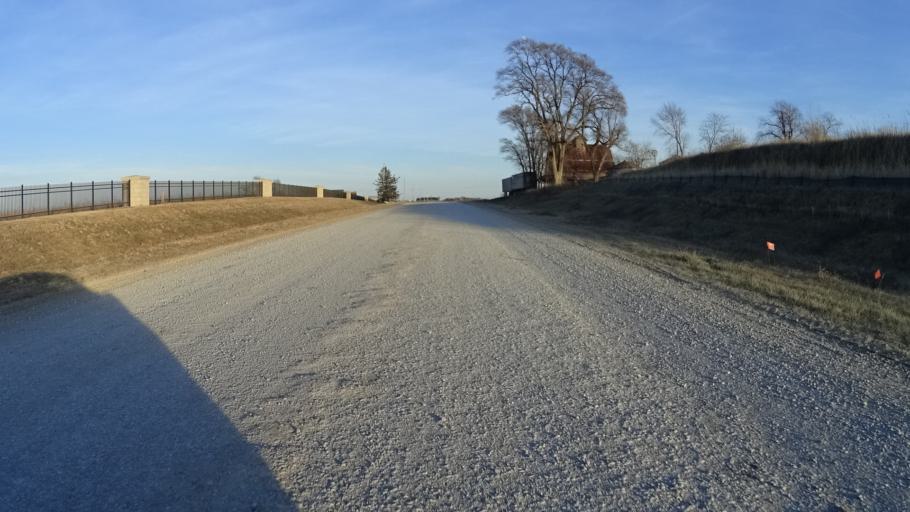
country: US
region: Nebraska
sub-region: Sarpy County
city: Springfield
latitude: 41.1325
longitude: -96.1330
